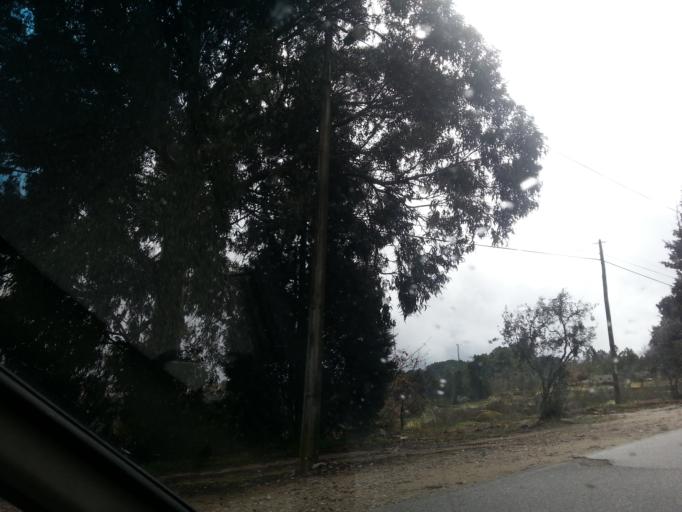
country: PT
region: Guarda
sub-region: Fornos de Algodres
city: Fornos de Algodres
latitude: 40.6219
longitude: -7.6051
